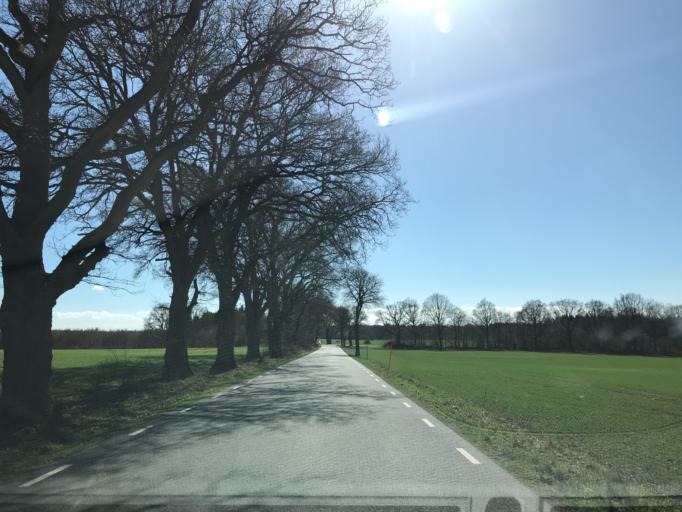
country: SE
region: Skane
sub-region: Svalovs Kommun
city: Kagerod
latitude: 55.9676
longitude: 13.0500
